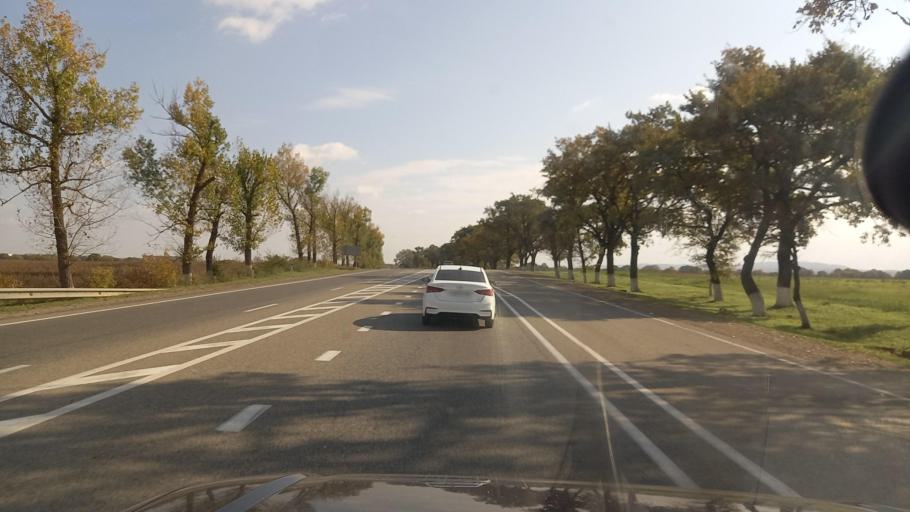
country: RU
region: Krasnodarskiy
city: Akhtyrskiy
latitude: 44.8544
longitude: 38.3366
